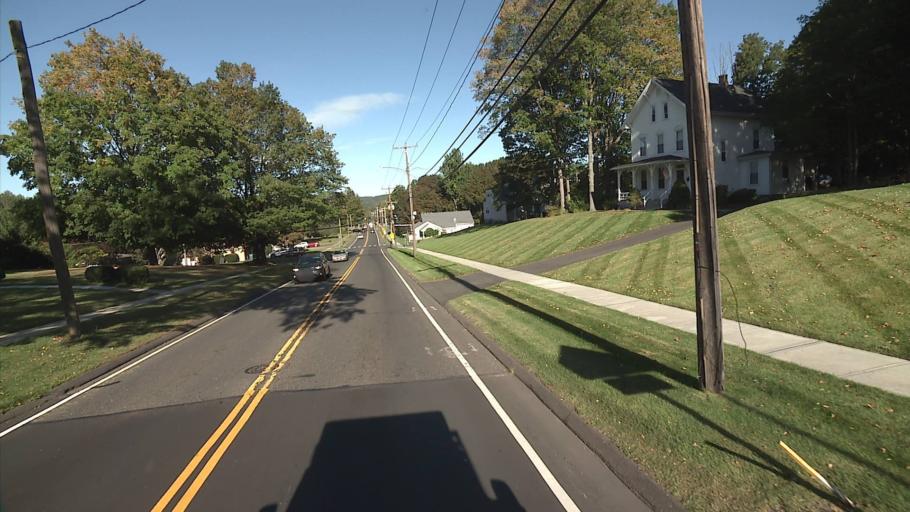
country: US
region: Connecticut
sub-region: New Haven County
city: Cheshire Village
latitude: 41.5050
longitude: -72.9057
